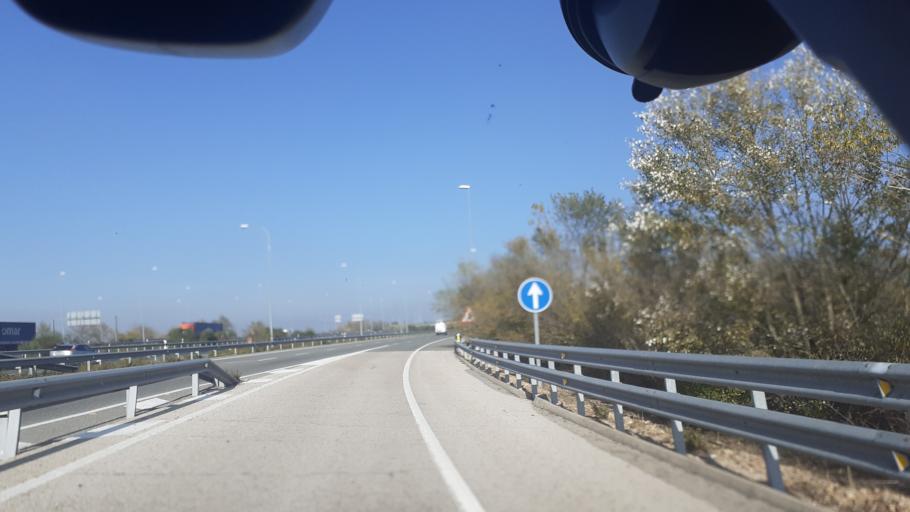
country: ES
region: Madrid
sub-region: Provincia de Madrid
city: Coslada
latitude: 40.4036
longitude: -3.5715
